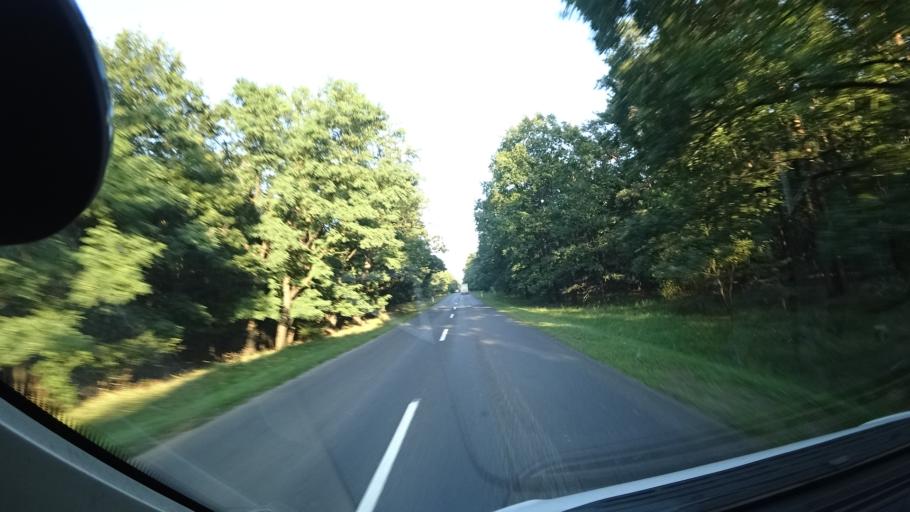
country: PL
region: Opole Voivodeship
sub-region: Powiat kedzierzynsko-kozielski
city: Dziergowice
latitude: 50.2807
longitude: 18.3393
